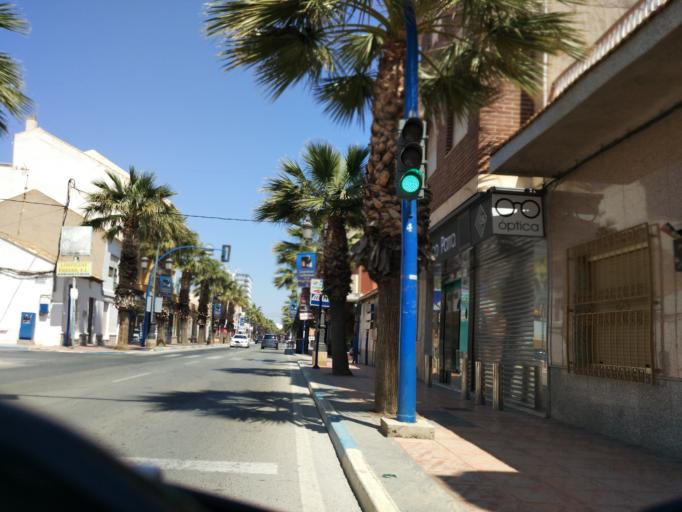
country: ES
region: Murcia
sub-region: Murcia
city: Los Alcazares
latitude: 37.7418
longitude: -0.8507
